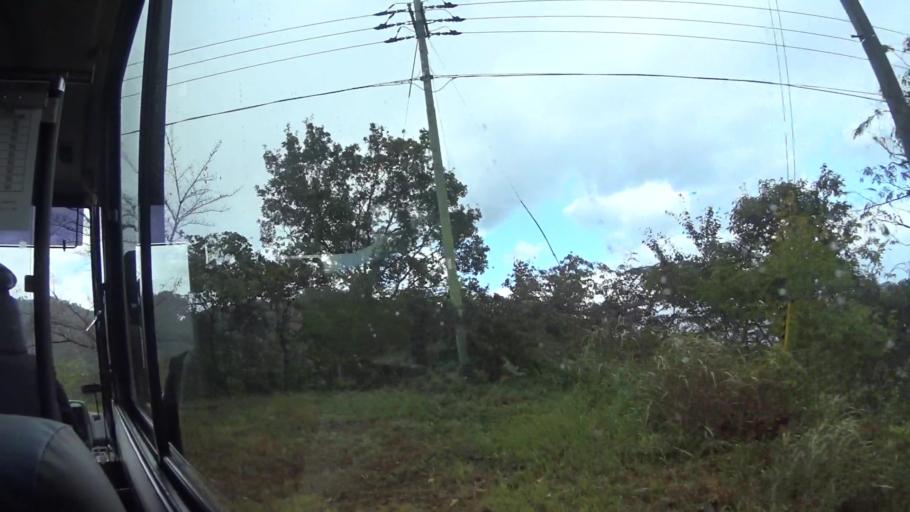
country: JP
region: Kyoto
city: Miyazu
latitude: 35.5899
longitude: 135.1896
